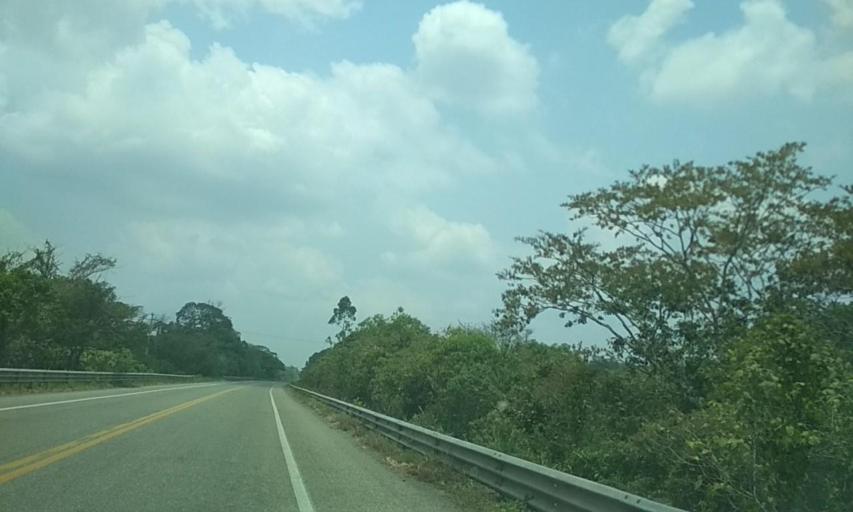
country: MX
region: Tabasco
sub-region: Huimanguillo
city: Francisco Rueda
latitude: 17.6488
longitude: -93.8342
